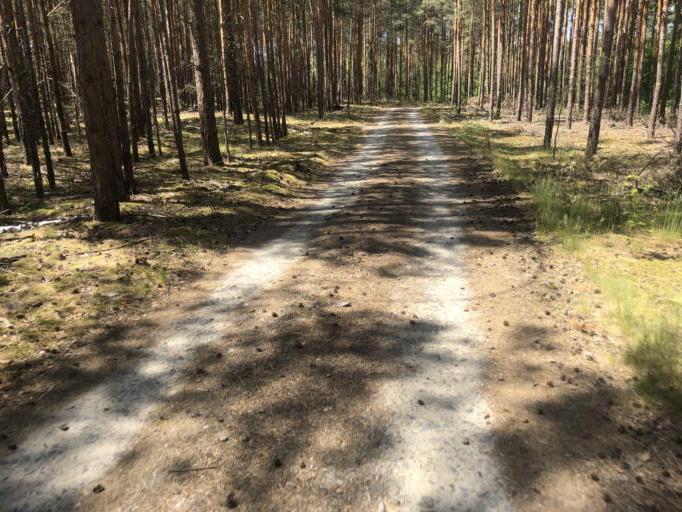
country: DE
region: Brandenburg
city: Gross Koris
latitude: 52.1946
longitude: 13.6501
